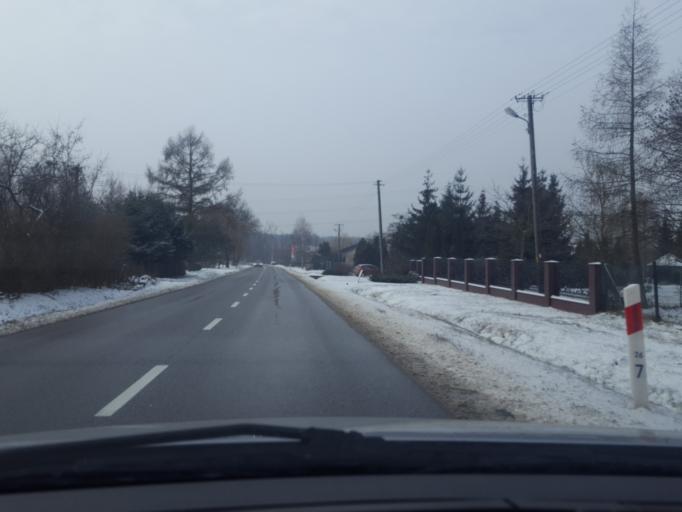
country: PL
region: Lodz Voivodeship
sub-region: Powiat brzezinski
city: Brzeziny
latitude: 51.8315
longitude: 19.7936
